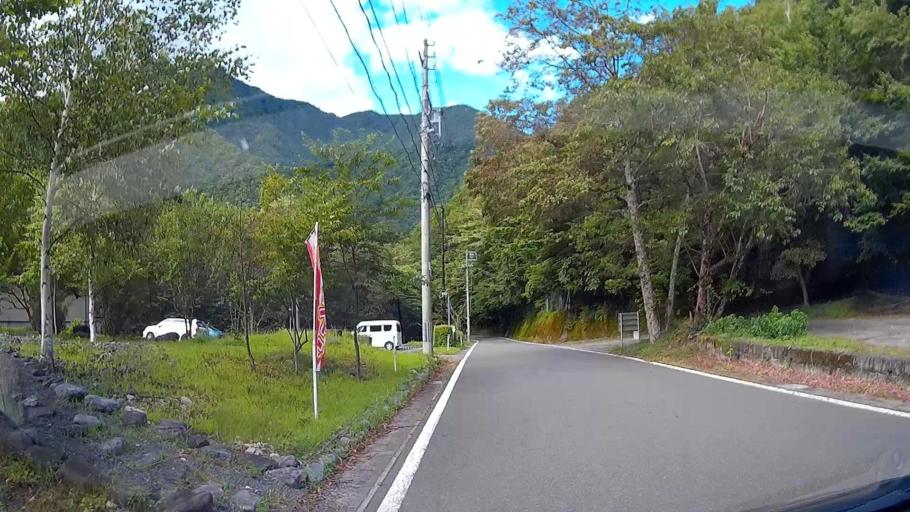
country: JP
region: Shizuoka
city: Shizuoka-shi
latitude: 35.3070
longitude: 138.1970
